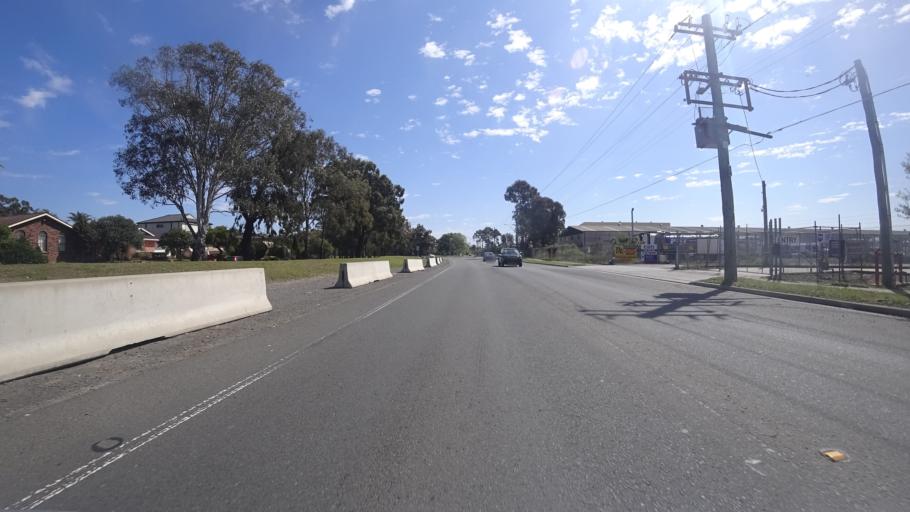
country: AU
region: New South Wales
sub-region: Fairfield
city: Chipping Norton
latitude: -33.9178
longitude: 150.9617
